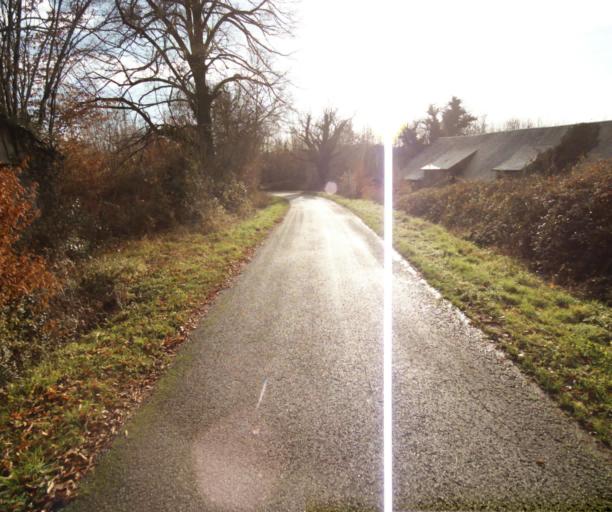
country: FR
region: Limousin
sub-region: Departement de la Correze
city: Sainte-Fereole
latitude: 45.2626
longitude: 1.5952
